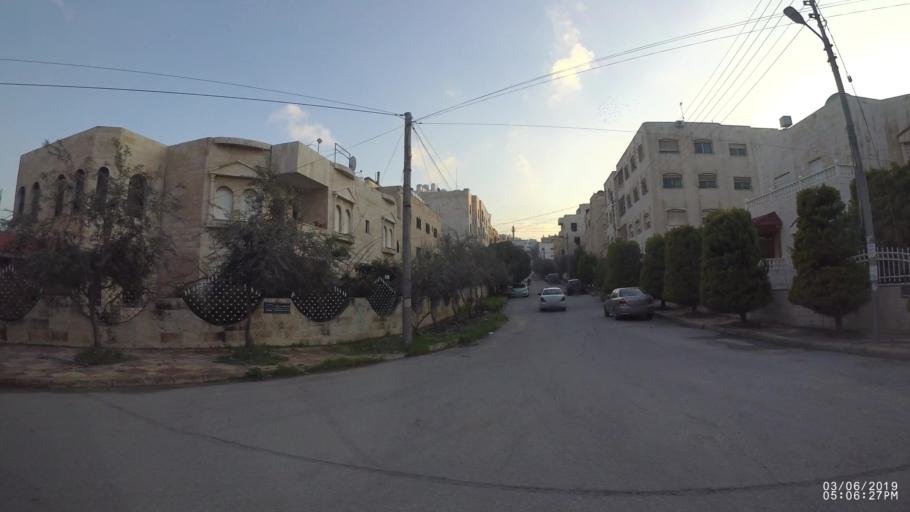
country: JO
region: Amman
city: Amman
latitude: 31.9925
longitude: 35.9468
